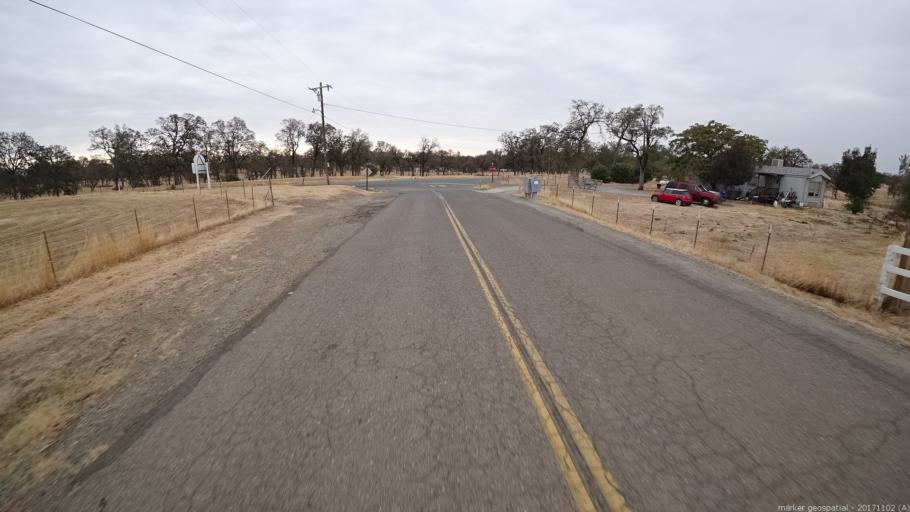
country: US
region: California
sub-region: Shasta County
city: Bella Vista
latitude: 40.6350
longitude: -122.2544
